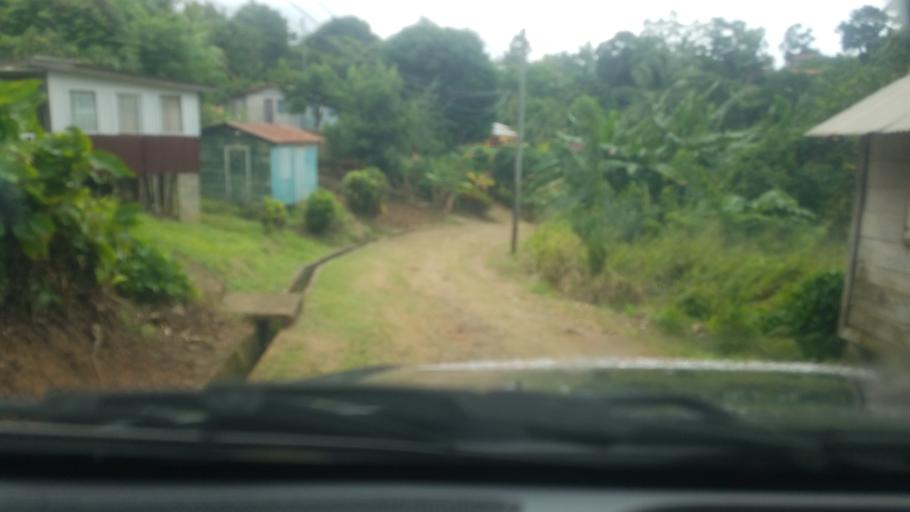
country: LC
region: Micoud Quarter
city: Micoud
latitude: 13.8040
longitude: -60.9490
